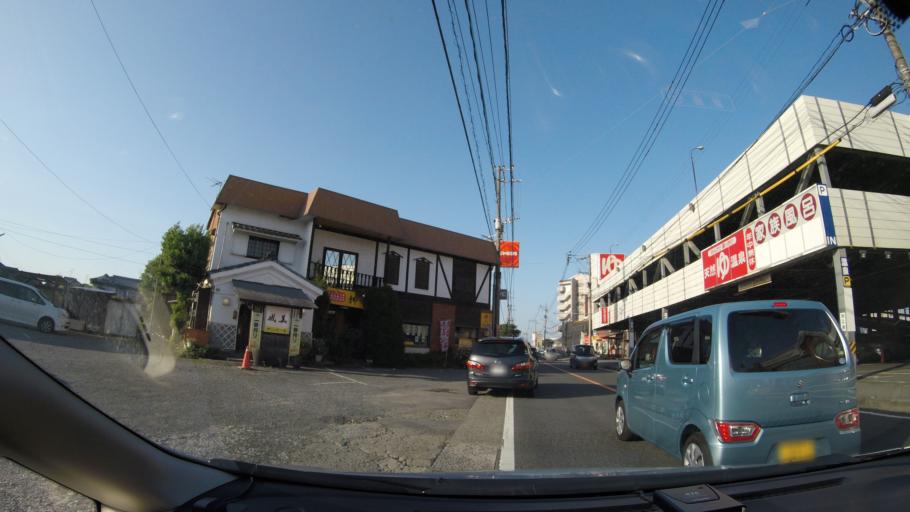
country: JP
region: Oita
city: Oita
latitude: 33.2084
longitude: 131.6048
